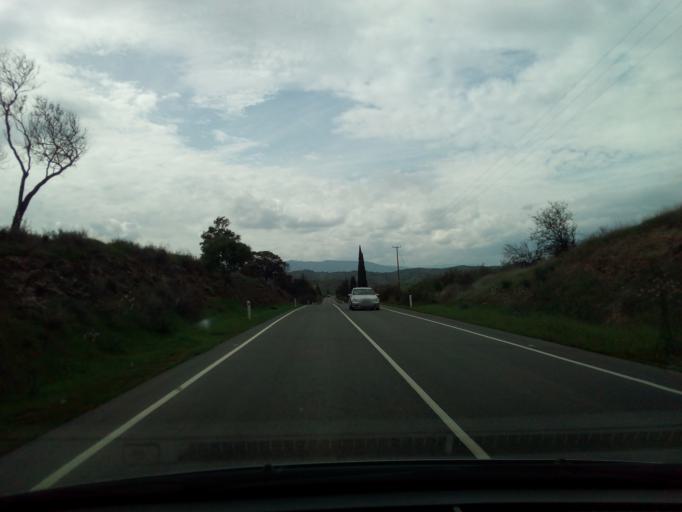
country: CY
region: Lefkosia
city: Astromeritis
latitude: 35.0880
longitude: 32.9610
